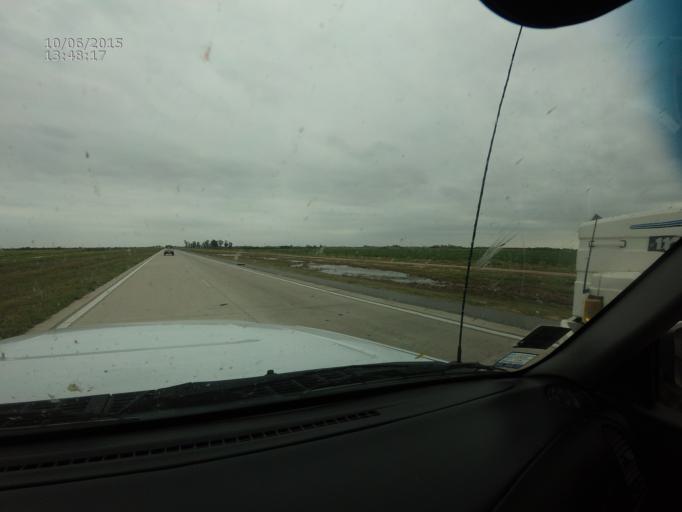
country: AR
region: Cordoba
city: Bell Ville
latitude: -32.5771
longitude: -62.6417
